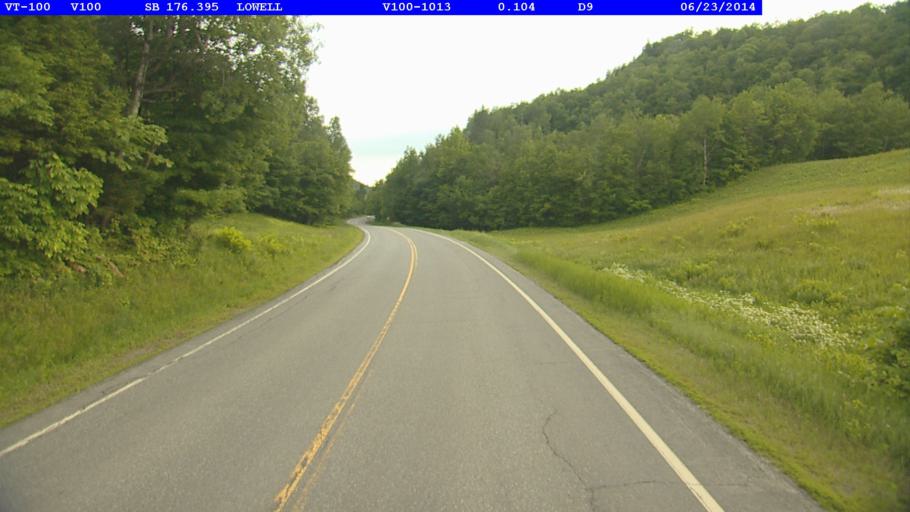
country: US
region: Vermont
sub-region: Lamoille County
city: Hyde Park
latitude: 44.7414
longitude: -72.4651
